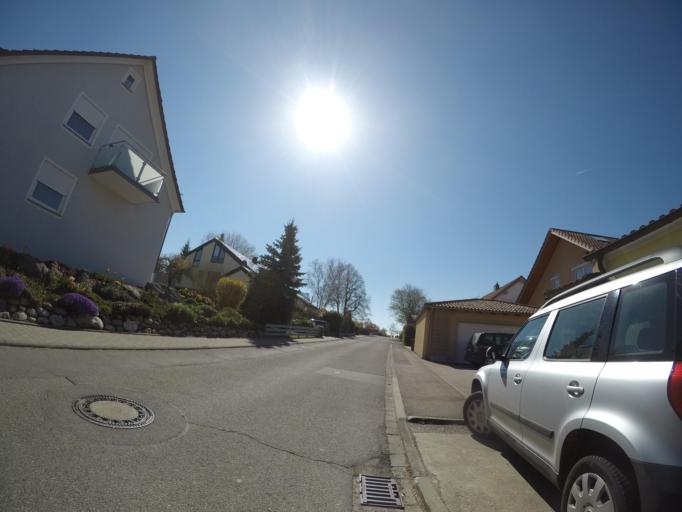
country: DE
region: Baden-Wuerttemberg
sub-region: Tuebingen Region
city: Wilhelmsdorf
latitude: 47.8648
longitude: 9.4280
